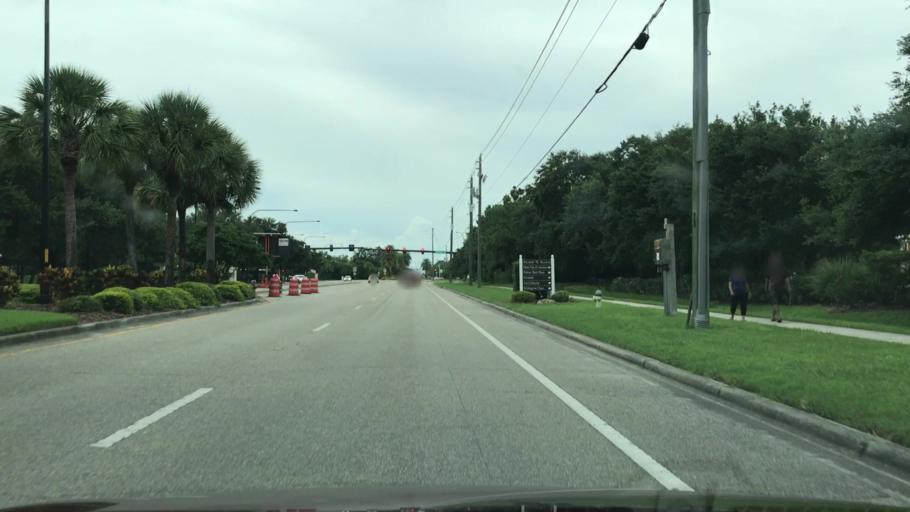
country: US
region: Florida
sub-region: Sarasota County
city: Bee Ridge
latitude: 27.2639
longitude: -82.4647
